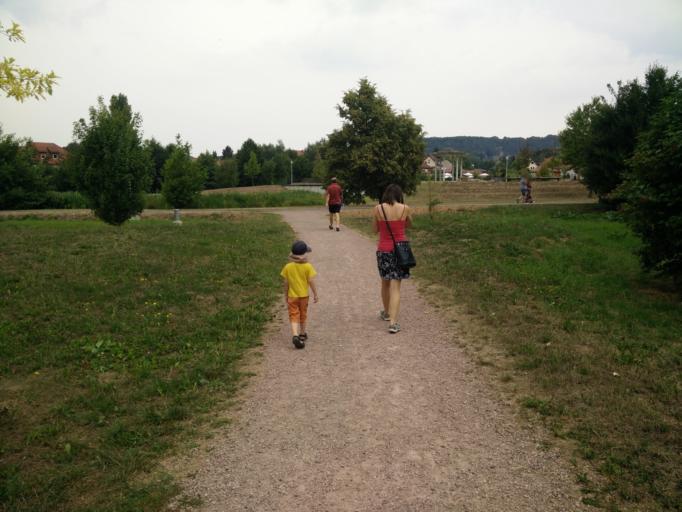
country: DE
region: Thuringia
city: Bad Liebenstein
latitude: 50.8135
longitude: 10.3493
